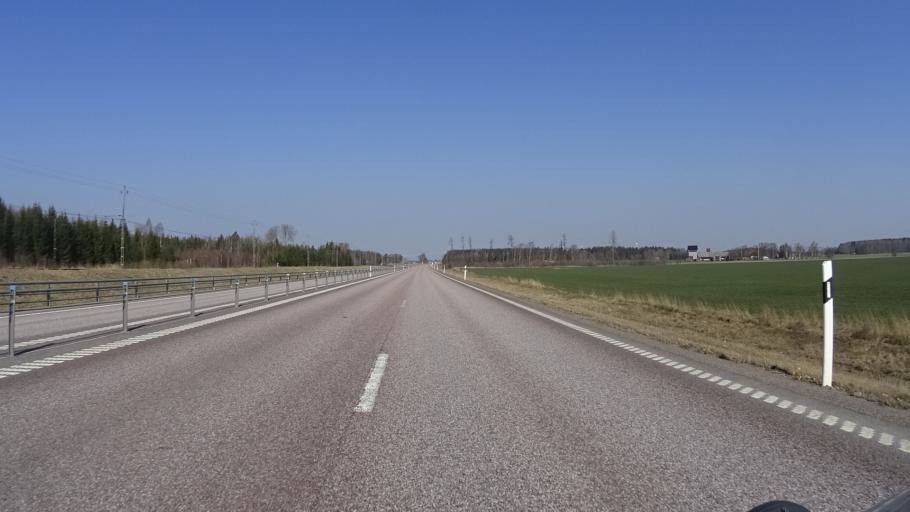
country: SE
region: OEstergoetland
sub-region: Motala Kommun
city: Stenstorp
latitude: 58.4150
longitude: 15.0759
